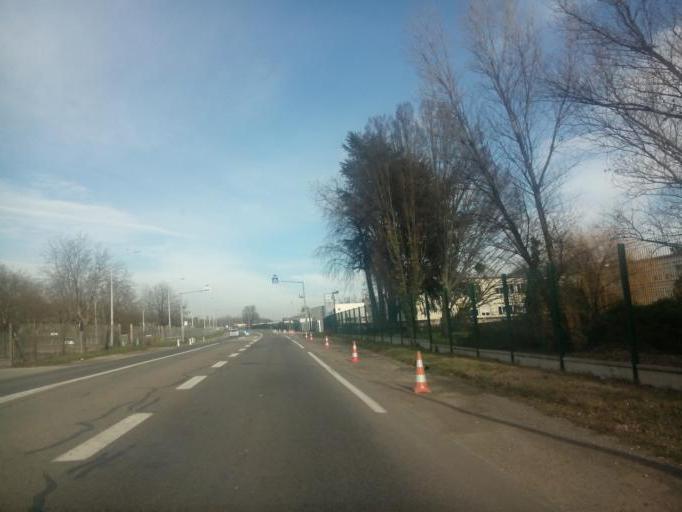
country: FR
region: Rhone-Alpes
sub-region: Departement du Rhone
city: Chaponost
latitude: 45.7010
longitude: 4.7673
